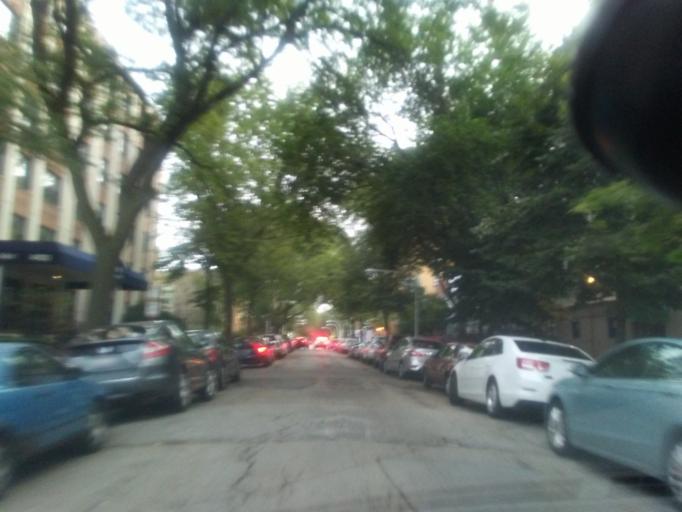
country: US
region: Illinois
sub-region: Cook County
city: Evanston
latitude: 41.9720
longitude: -87.6563
